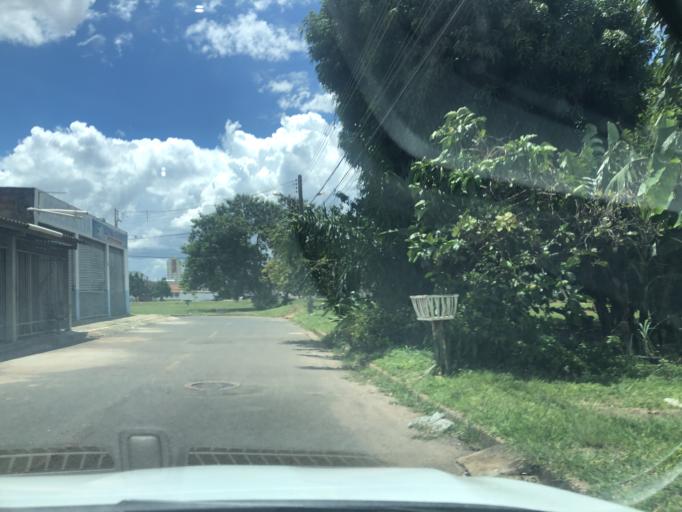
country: BR
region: Federal District
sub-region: Brasilia
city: Brasilia
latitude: -15.8698
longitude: -48.0658
